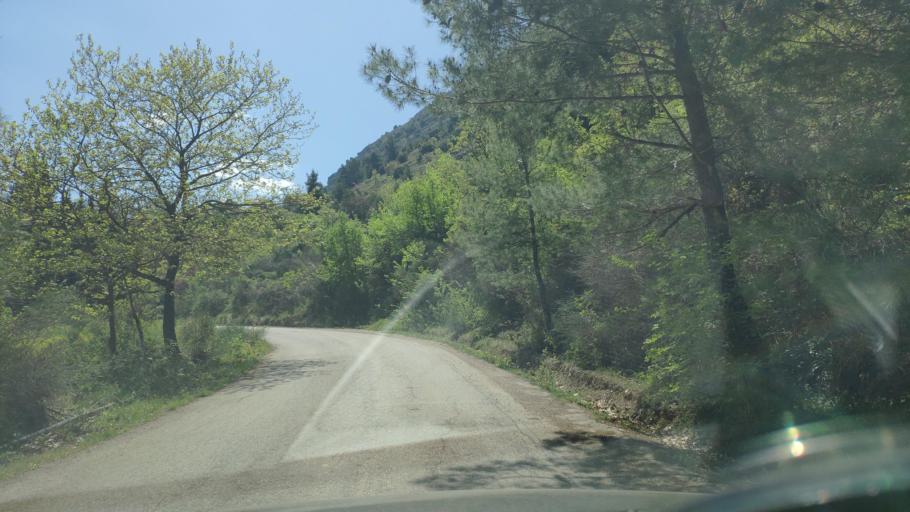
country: GR
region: West Greece
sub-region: Nomos Achaias
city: Aiyira
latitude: 38.0687
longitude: 22.3332
